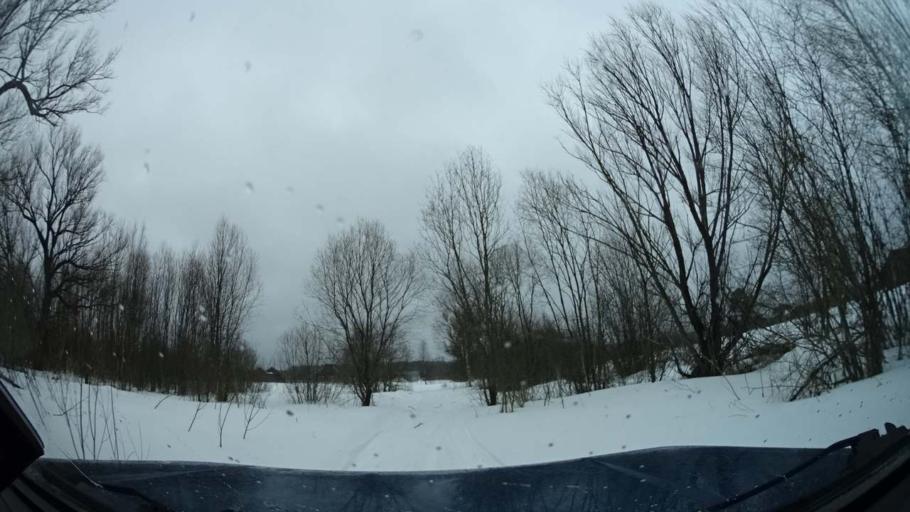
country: RU
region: Tverskaya
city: Gorodnya
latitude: 56.8290
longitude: 36.3997
